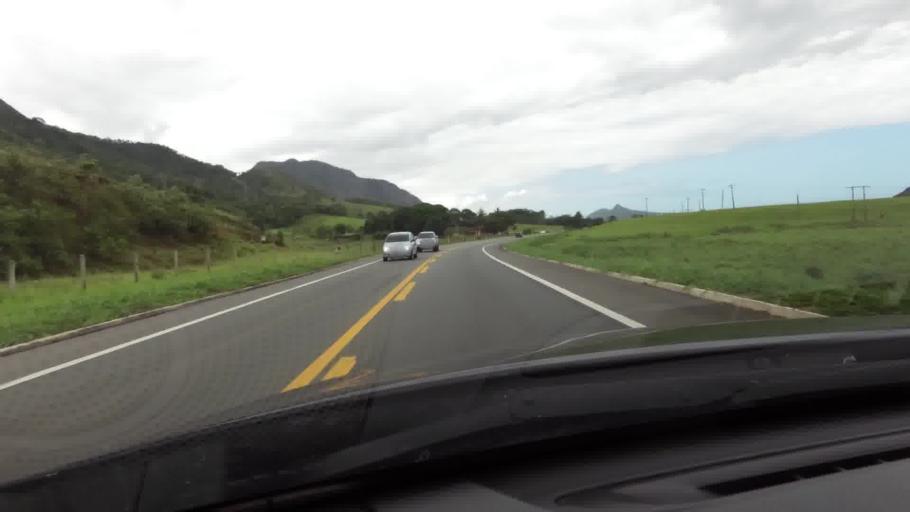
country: BR
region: Espirito Santo
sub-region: Guarapari
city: Guarapari
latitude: -20.6178
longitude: -40.5167
